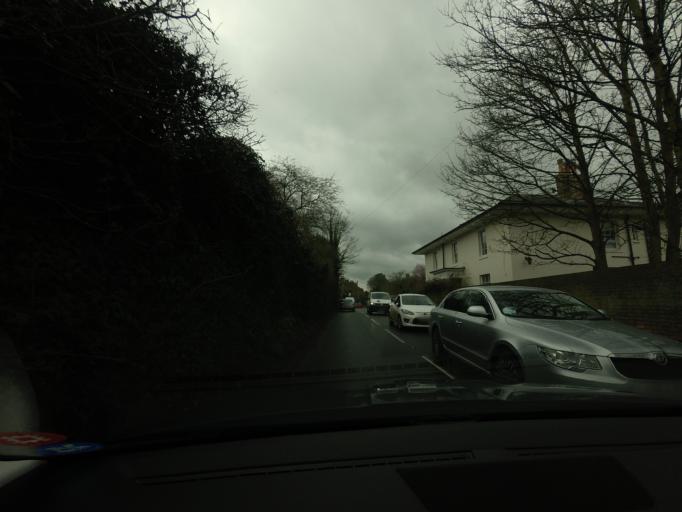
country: GB
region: England
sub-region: Kent
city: Eynsford
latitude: 51.3727
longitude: 0.2189
